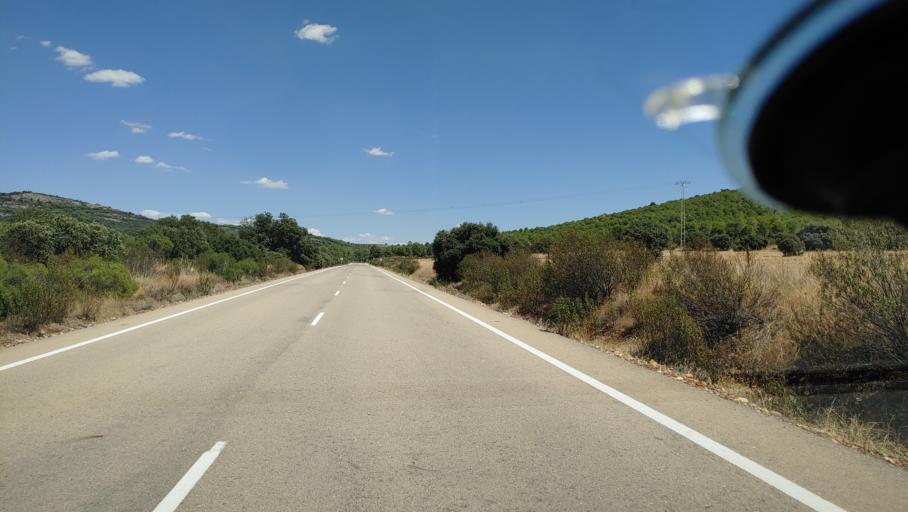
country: ES
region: Castille-La Mancha
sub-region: Provincia de Ciudad Real
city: Saceruela
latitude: 38.9873
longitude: -4.5481
